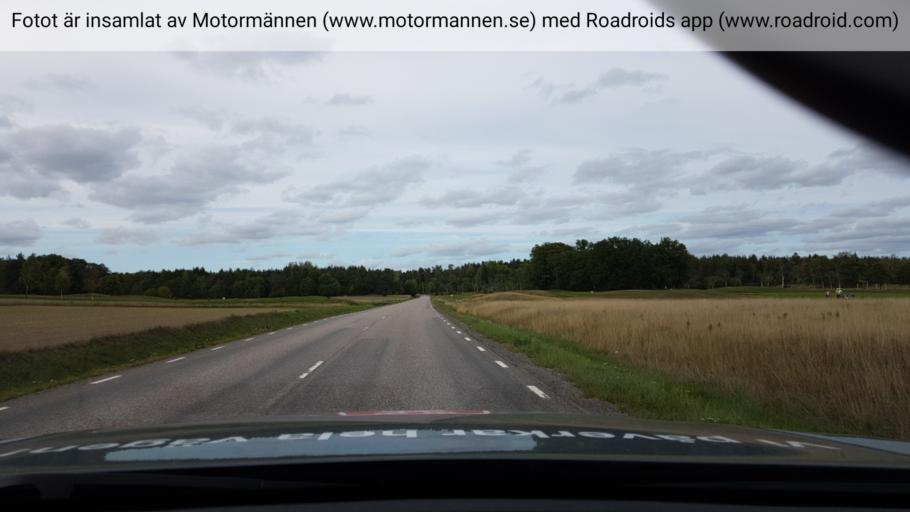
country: SE
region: Stockholm
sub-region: Haninge Kommun
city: Haninge
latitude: 59.1096
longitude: 18.1887
